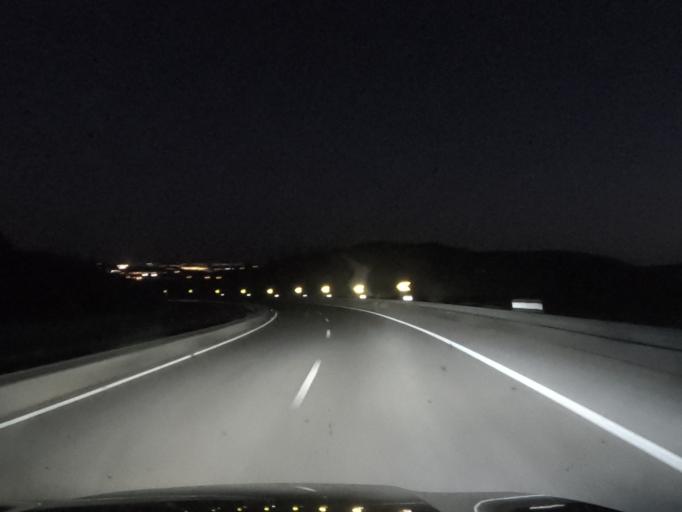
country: PT
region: Faro
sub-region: Loule
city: Loule
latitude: 37.1405
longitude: -8.0445
